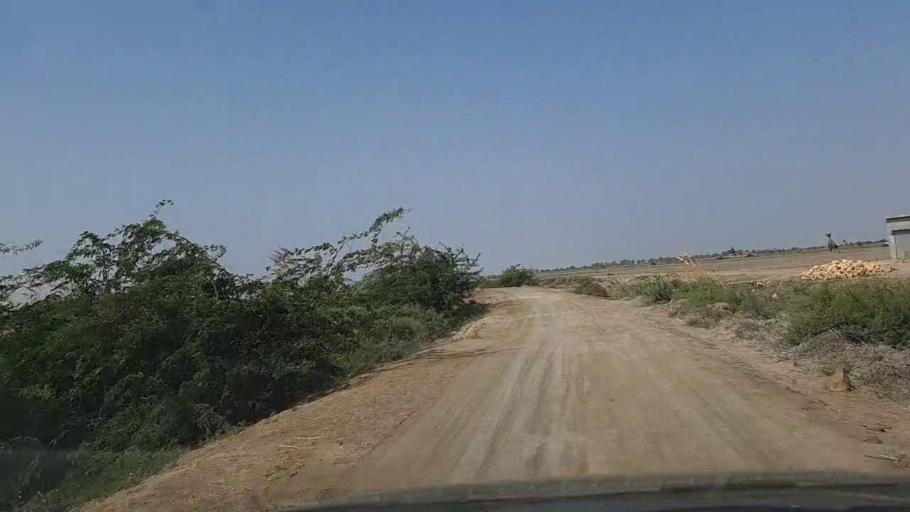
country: PK
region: Sindh
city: Gharo
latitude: 24.7043
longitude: 67.5820
